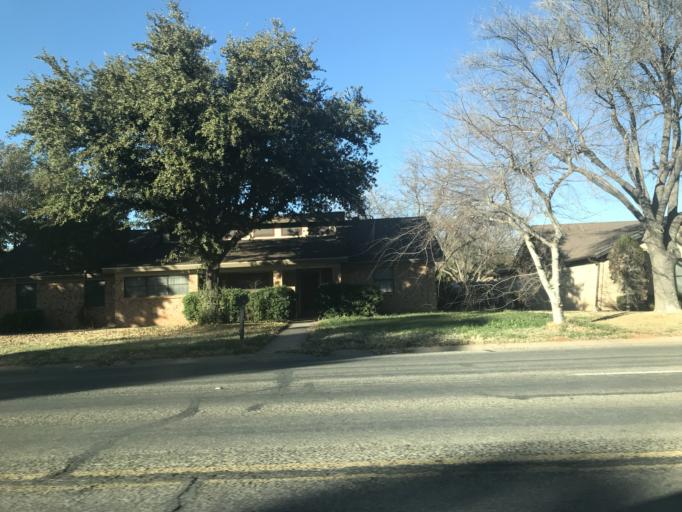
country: US
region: Texas
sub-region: Tom Green County
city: San Angelo
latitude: 31.4277
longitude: -100.4936
